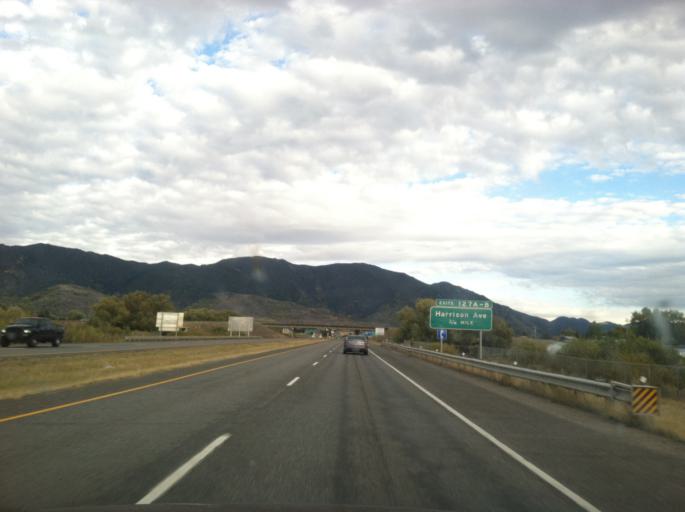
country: US
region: Montana
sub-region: Silver Bow County
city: Butte
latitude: 45.9898
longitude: -112.5249
